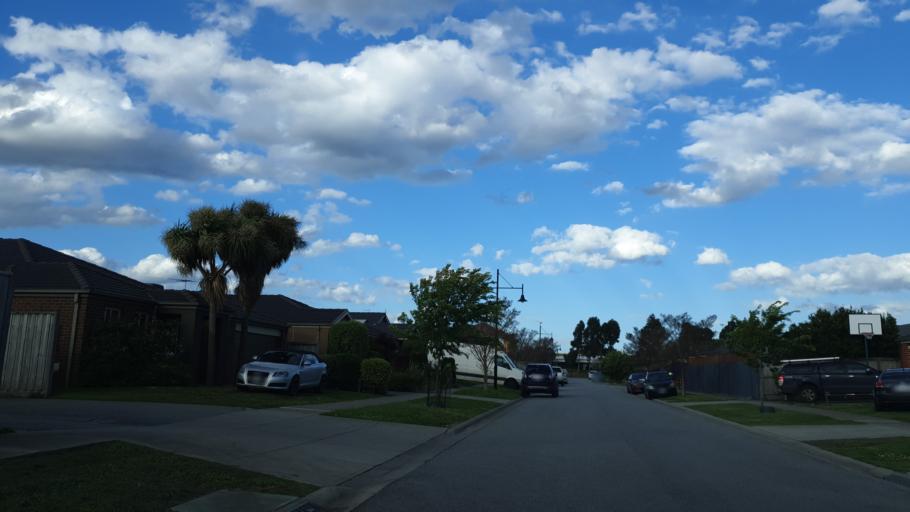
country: AU
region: Victoria
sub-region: Casey
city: Cranbourne North
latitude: -38.0879
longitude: 145.2865
